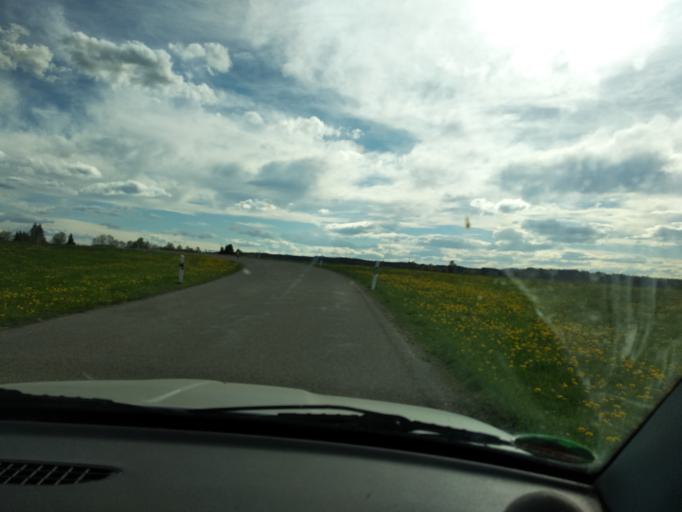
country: DE
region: Bavaria
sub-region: Swabia
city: Lachen
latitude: 47.9341
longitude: 10.2323
